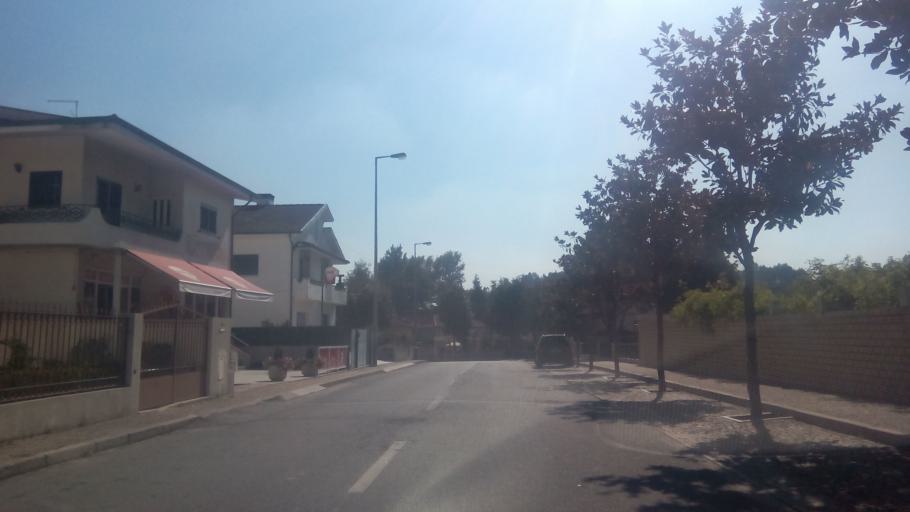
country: PT
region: Porto
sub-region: Paredes
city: Madalena
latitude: 41.2169
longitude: -8.3352
